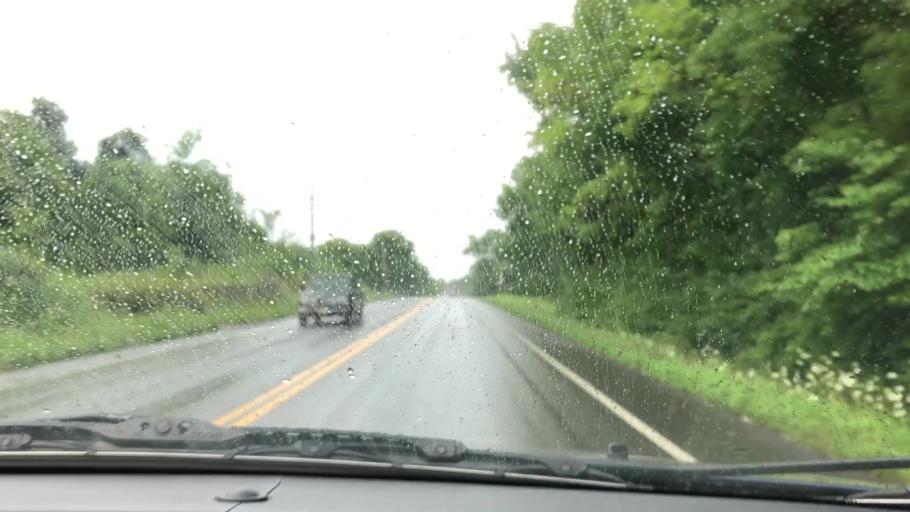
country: US
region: Tennessee
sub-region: Williamson County
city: Franklin
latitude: 35.9012
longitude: -86.9130
